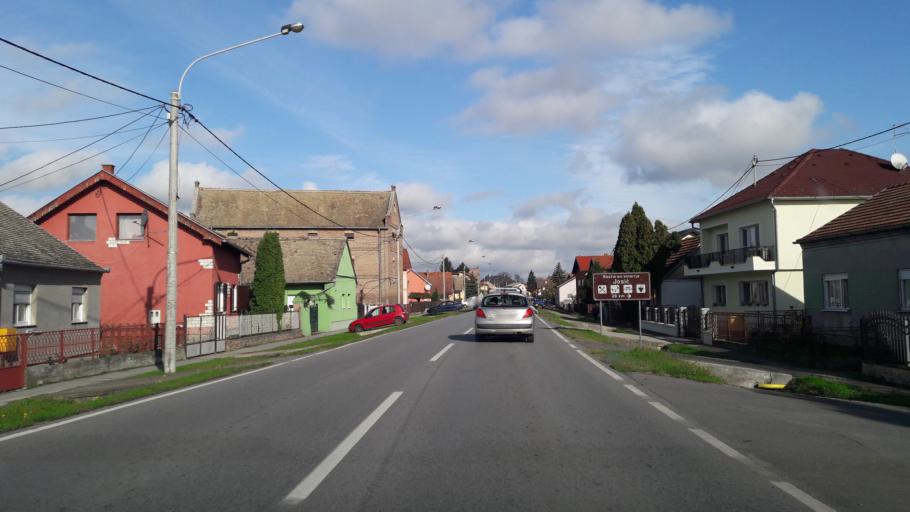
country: HR
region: Osjecko-Baranjska
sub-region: Grad Osijek
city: Bilje
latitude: 45.5990
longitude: 18.7428
